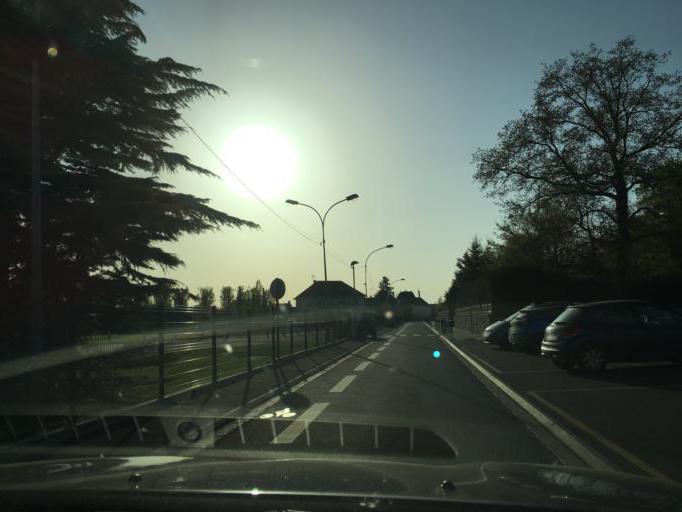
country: FR
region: Centre
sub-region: Departement du Loir-et-Cher
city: Ouzouer-le-Marche
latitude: 47.9085
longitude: 1.5303
